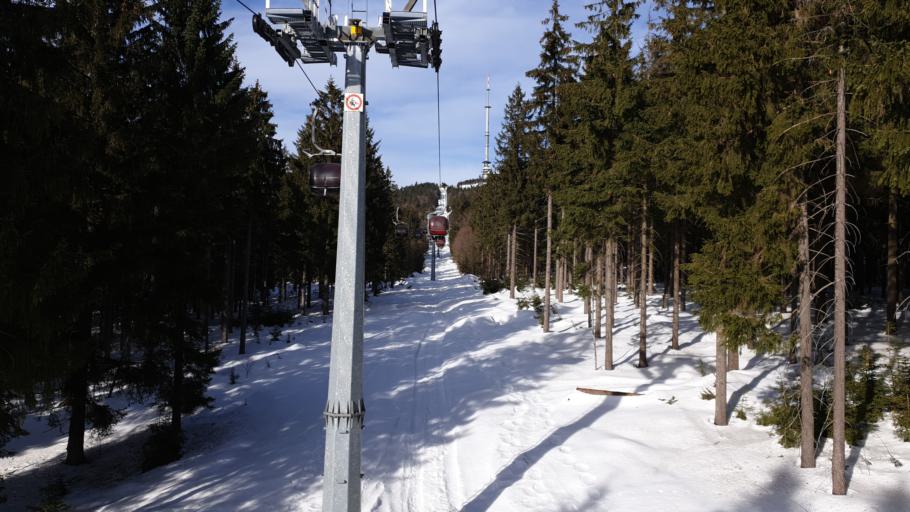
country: DE
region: Bavaria
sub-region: Upper Franconia
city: Bischofsgrun
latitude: 50.0195
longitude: 11.8083
